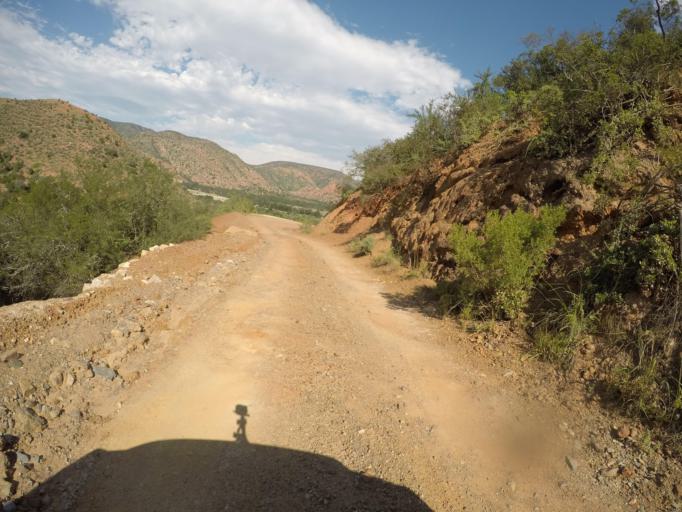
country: ZA
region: Eastern Cape
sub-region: Cacadu District Municipality
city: Kareedouw
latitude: -33.6580
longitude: 24.4010
